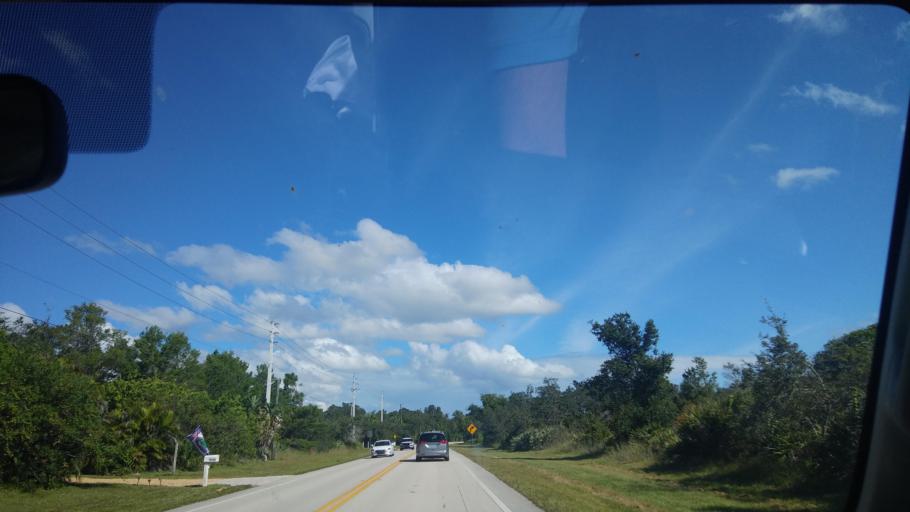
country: US
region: Florida
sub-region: Indian River County
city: Roseland
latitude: 27.8214
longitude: -80.5045
